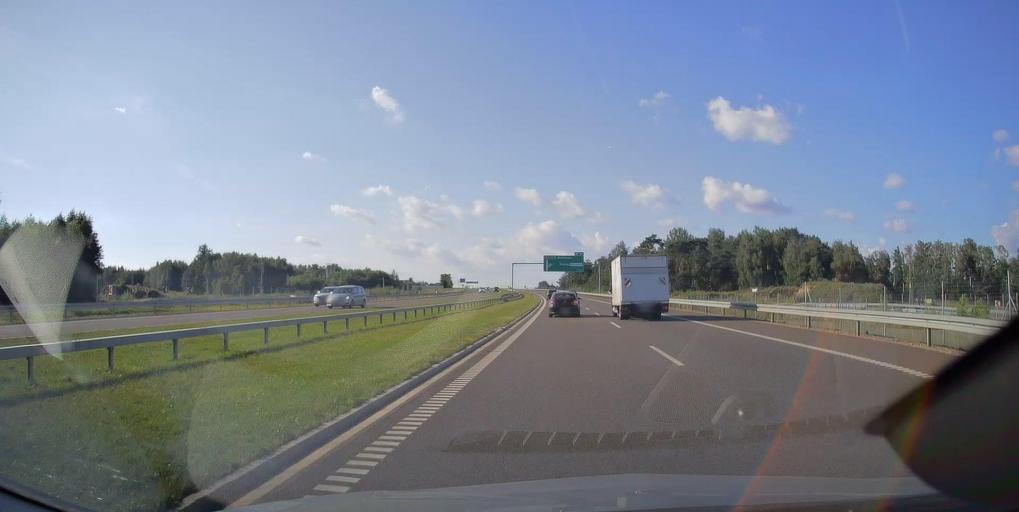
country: PL
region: Masovian Voivodeship
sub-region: Powiat radomski
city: Jedlinsk
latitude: 51.5253
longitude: 21.0844
